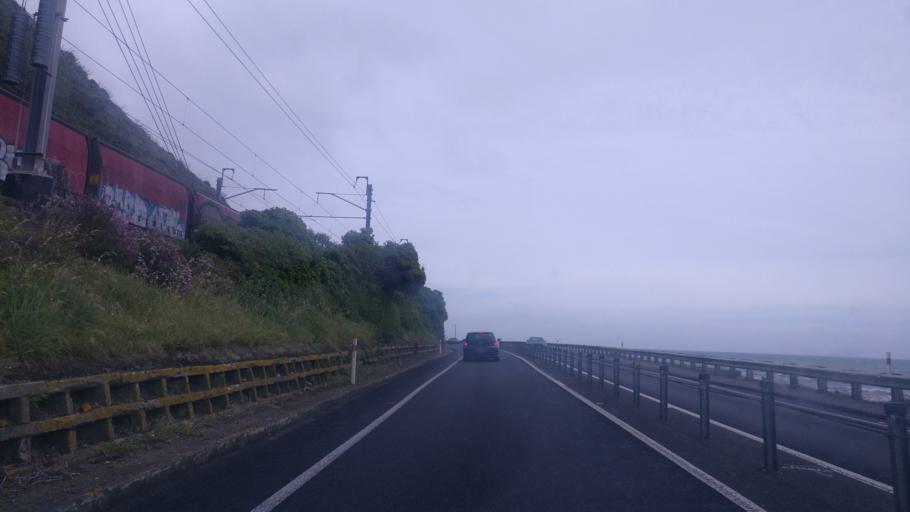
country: NZ
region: Wellington
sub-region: Kapiti Coast District
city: Paraparaumu
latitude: -41.0049
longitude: 174.9292
